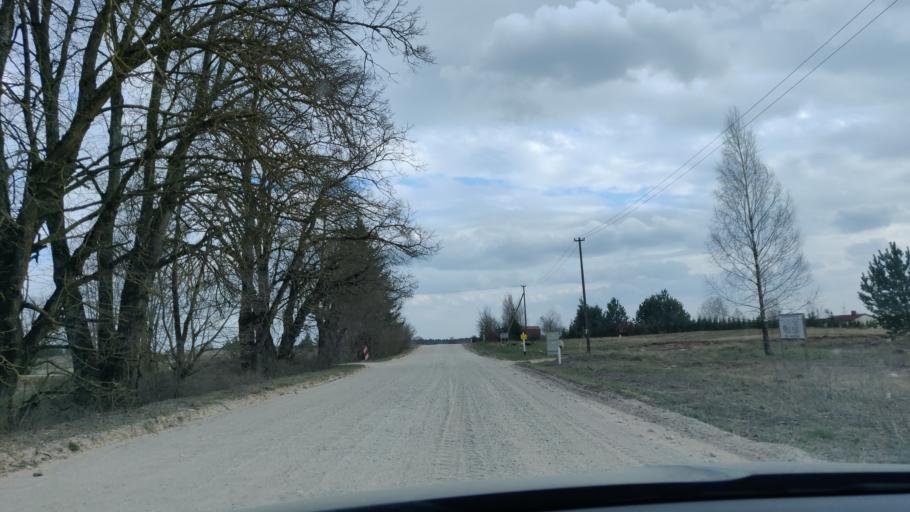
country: LT
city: Lentvaris
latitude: 54.6158
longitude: 25.0682
